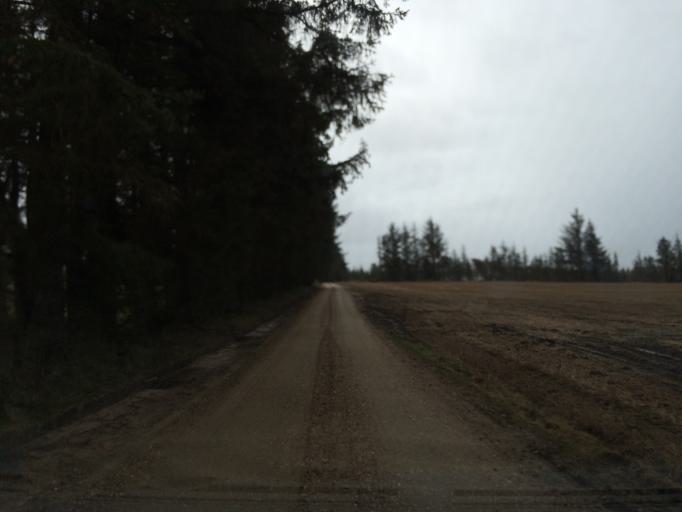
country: DK
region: Central Jutland
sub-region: Holstebro Kommune
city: Ulfborg
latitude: 56.2264
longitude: 8.4945
